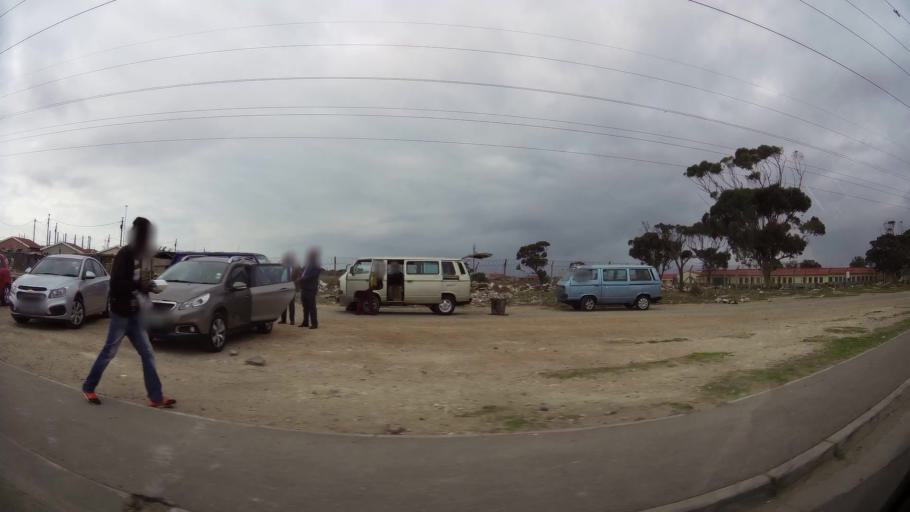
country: ZA
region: Eastern Cape
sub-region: Nelson Mandela Bay Metropolitan Municipality
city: Port Elizabeth
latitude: -33.8790
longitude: 25.5848
